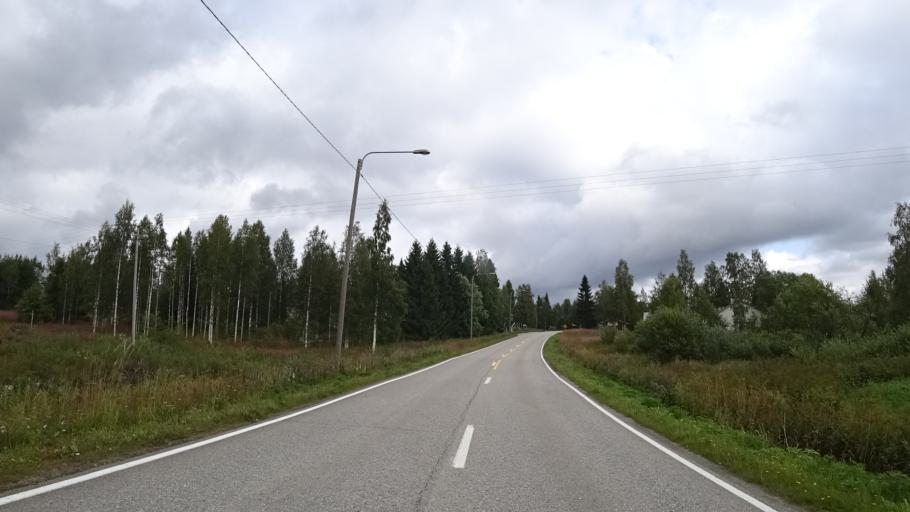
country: FI
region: North Karelia
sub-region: Joensuu
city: Ilomantsi
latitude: 62.9306
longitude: 31.2789
